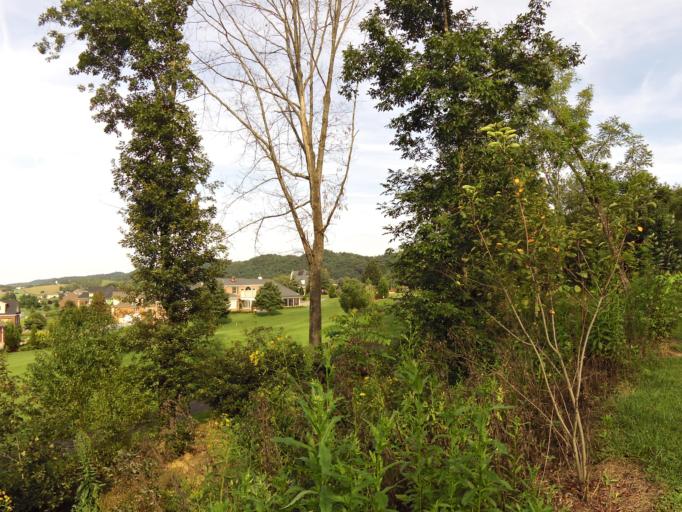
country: US
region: Virginia
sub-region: Washington County
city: Abingdon
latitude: 36.6985
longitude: -81.9525
